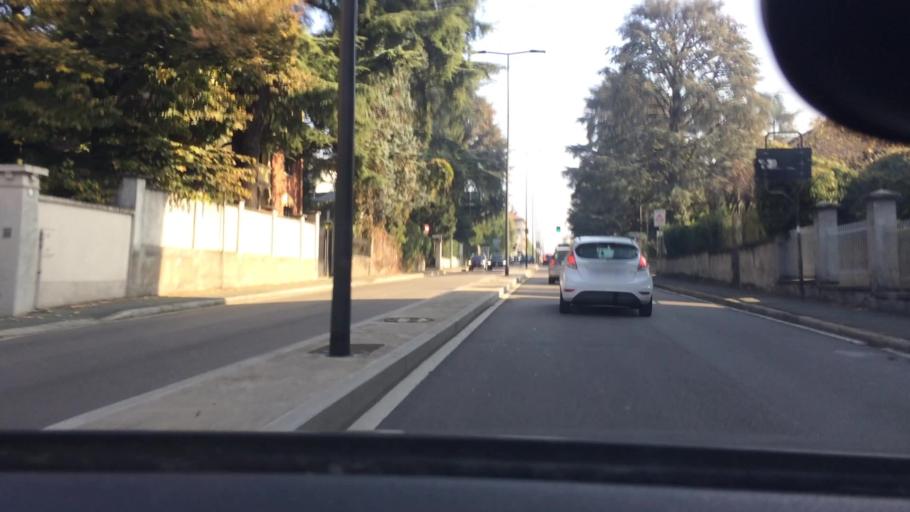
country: IT
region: Lombardy
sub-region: Citta metropolitana di Milano
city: San Vittore Olona
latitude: 45.5940
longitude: 8.9340
